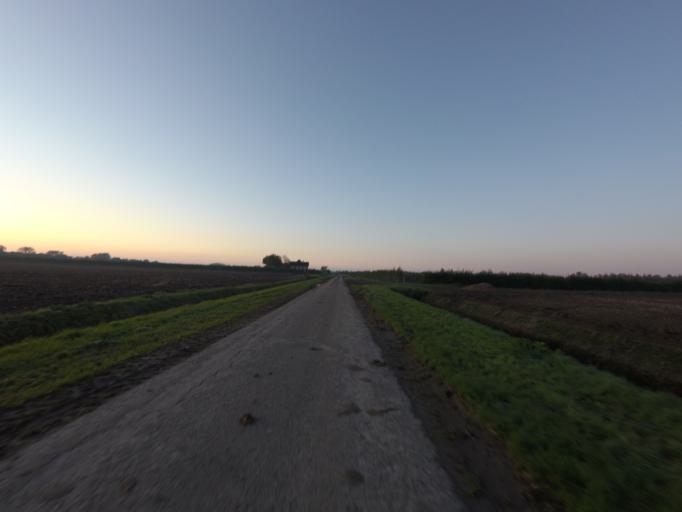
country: NL
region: North Brabant
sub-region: Gemeente Woudrichem
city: Almkerk
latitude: 51.7815
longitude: 4.9770
